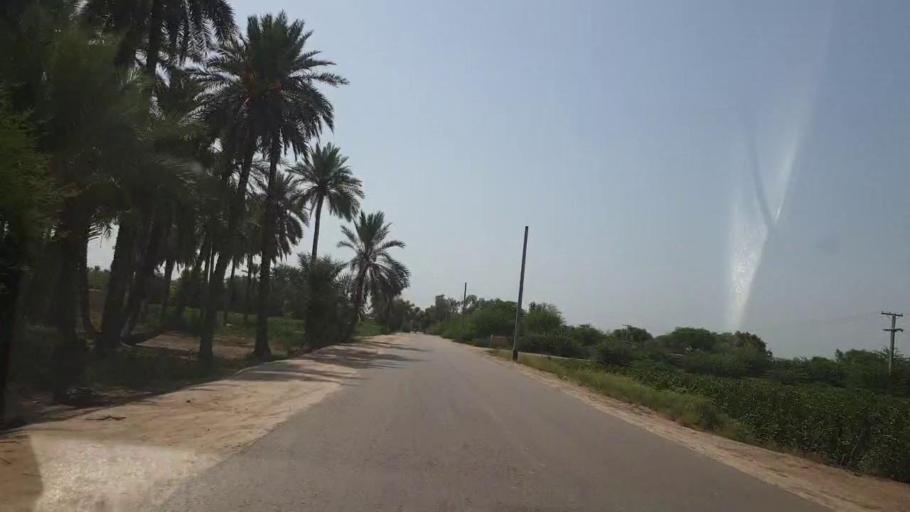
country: PK
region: Sindh
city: Bozdar
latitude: 27.1212
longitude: 68.5481
